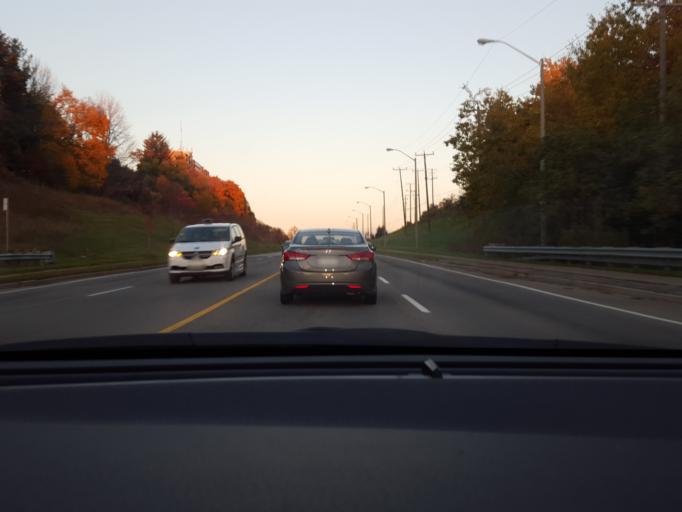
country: CA
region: Ontario
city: Scarborough
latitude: 43.7814
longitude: -79.2102
